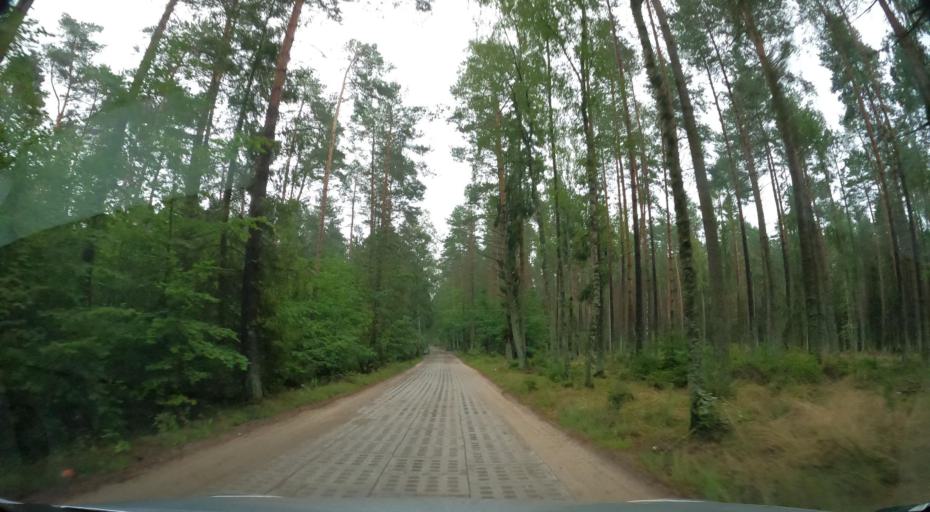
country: PL
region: Pomeranian Voivodeship
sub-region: Powiat kartuski
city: Chwaszczyno
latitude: 54.4189
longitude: 18.4269
